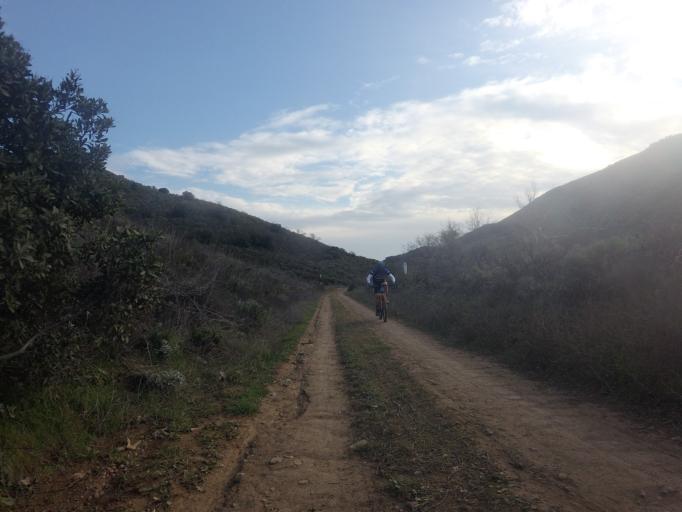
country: US
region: California
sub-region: Riverside County
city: Corona
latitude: 33.8081
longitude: -117.6524
